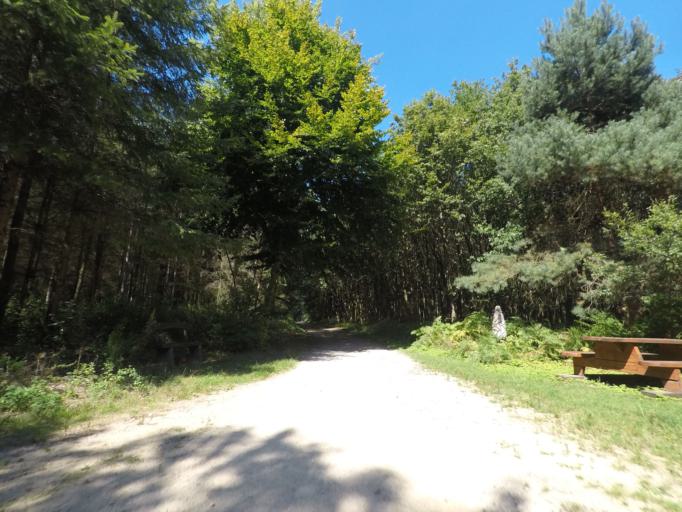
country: LU
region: Luxembourg
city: Bereldange
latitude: 49.6387
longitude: 6.1107
